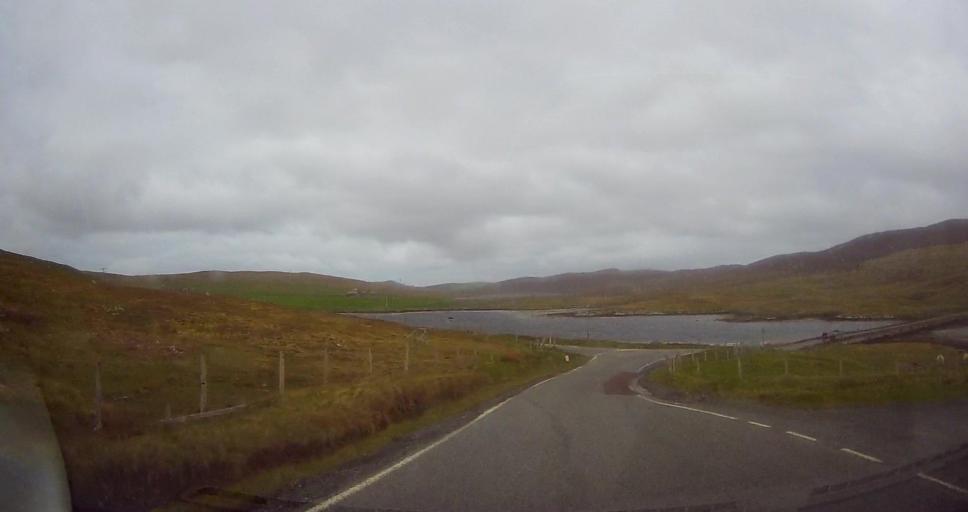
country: GB
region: Scotland
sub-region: Shetland Islands
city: Sandwick
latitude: 60.2432
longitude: -1.5322
